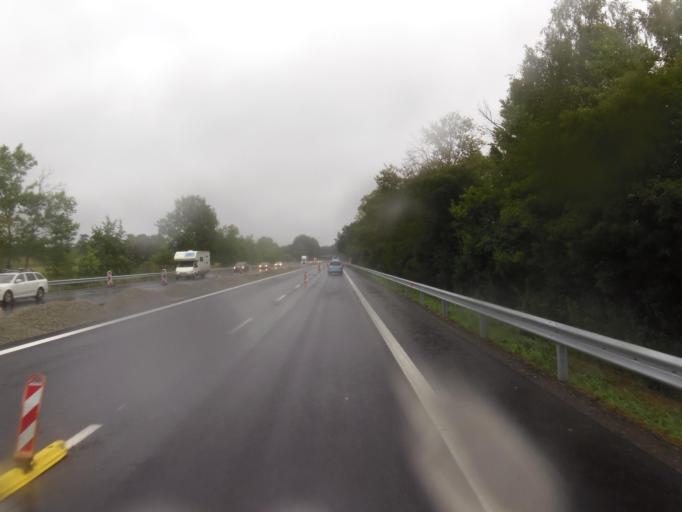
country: CZ
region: Jihocesky
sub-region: Okres Jindrichuv Hradec
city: Trebon
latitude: 49.0121
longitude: 14.7752
